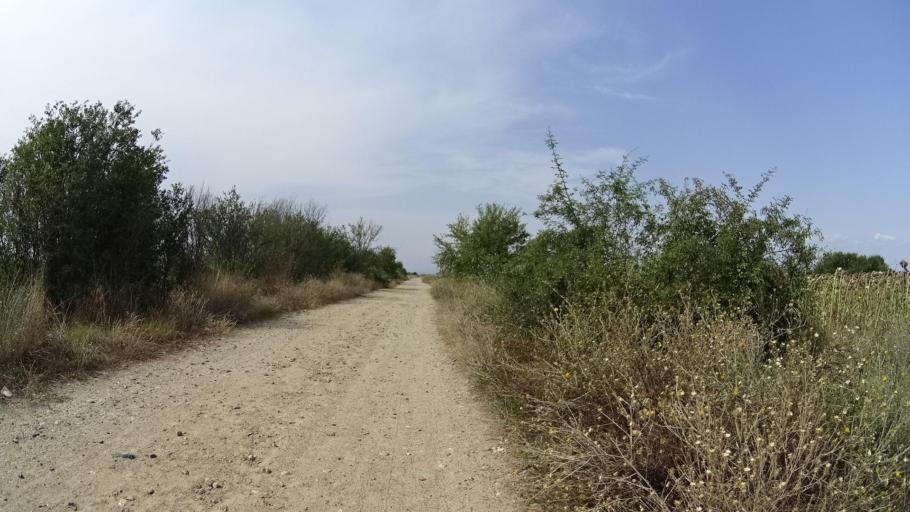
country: BG
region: Plovdiv
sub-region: Obshtina Kaloyanovo
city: Kaloyanovo
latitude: 42.2838
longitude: 24.7981
